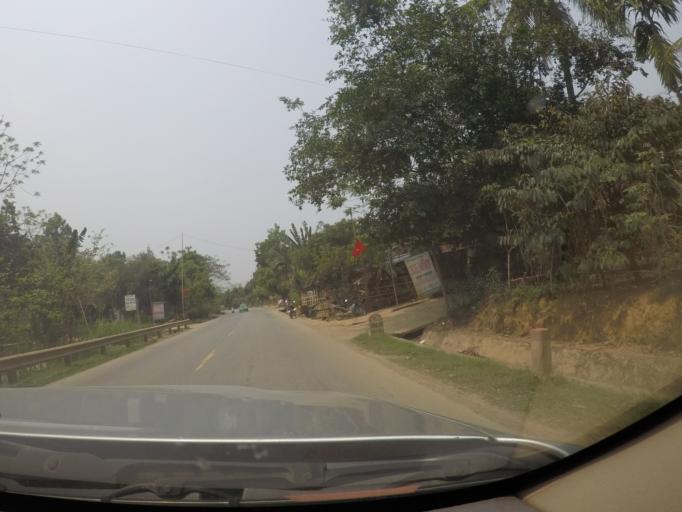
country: VN
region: Thanh Hoa
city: Thi Tran Ngoc Lac
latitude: 20.1300
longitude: 105.4042
